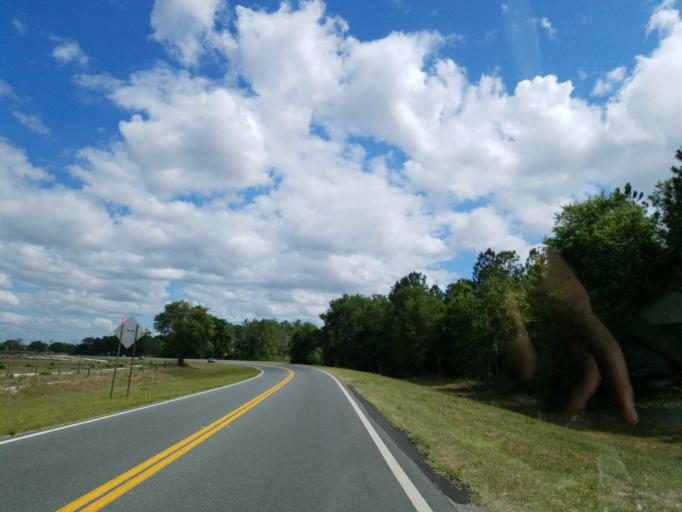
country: US
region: Florida
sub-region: Sumter County
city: Lake Panasoffkee
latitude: 28.7514
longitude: -82.0949
